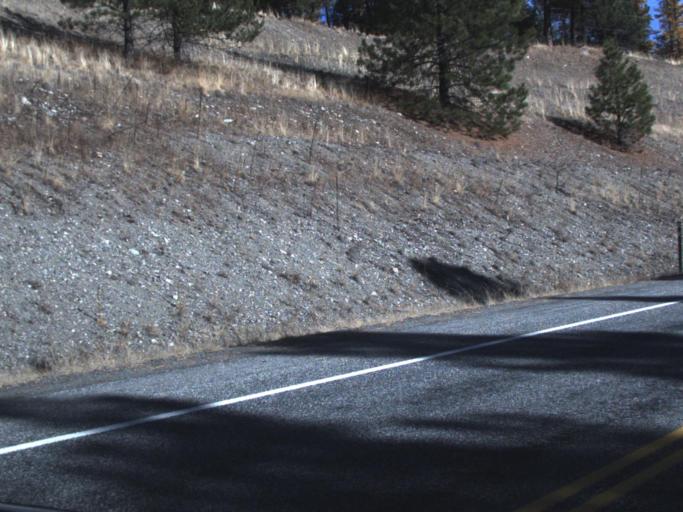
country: US
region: Washington
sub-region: Ferry County
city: Republic
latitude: 48.6549
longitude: -118.7974
